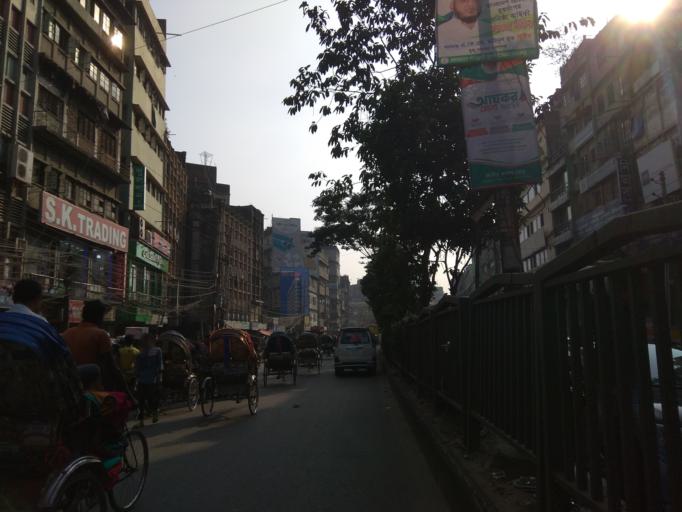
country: BD
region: Dhaka
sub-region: Dhaka
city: Dhaka
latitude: 23.7212
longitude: 90.4105
